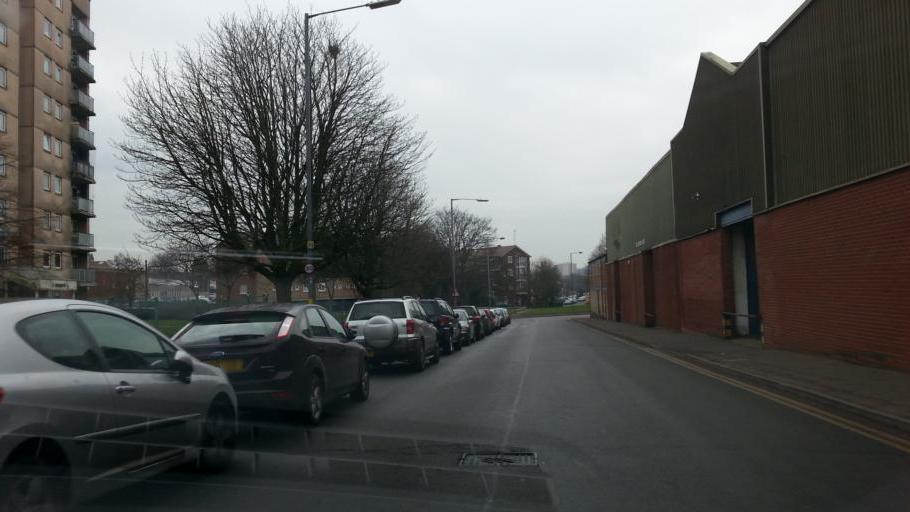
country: GB
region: England
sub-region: City and Borough of Birmingham
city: Birmingham
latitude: 52.4701
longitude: -1.8861
